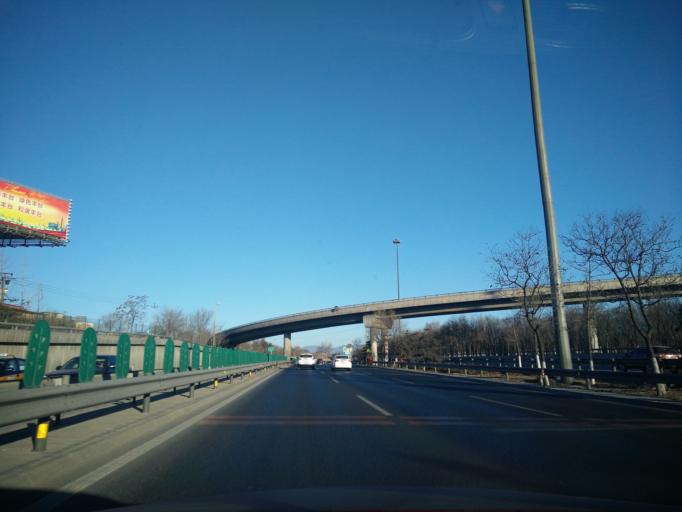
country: CN
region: Beijing
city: Lugu
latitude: 39.8452
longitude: 116.2181
